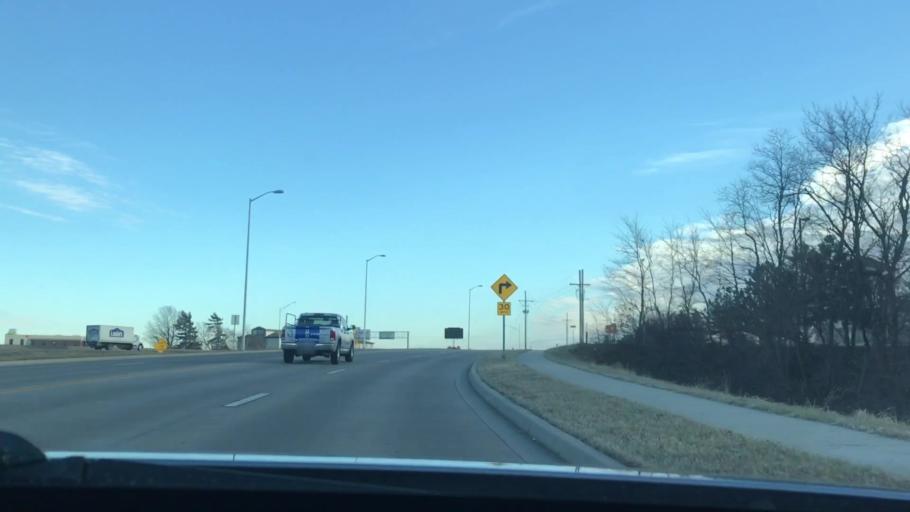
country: US
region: Missouri
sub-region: Platte County
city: Weatherby Lake
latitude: 39.2715
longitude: -94.6693
